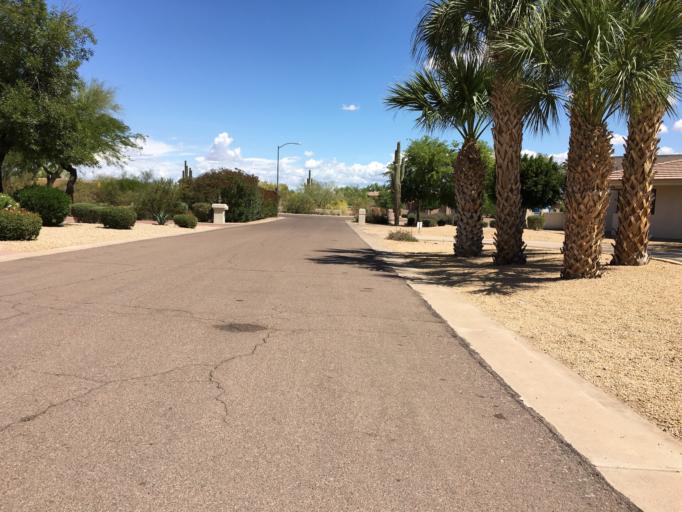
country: US
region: Arizona
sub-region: Maricopa County
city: Paradise Valley
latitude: 33.5728
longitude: -111.9914
